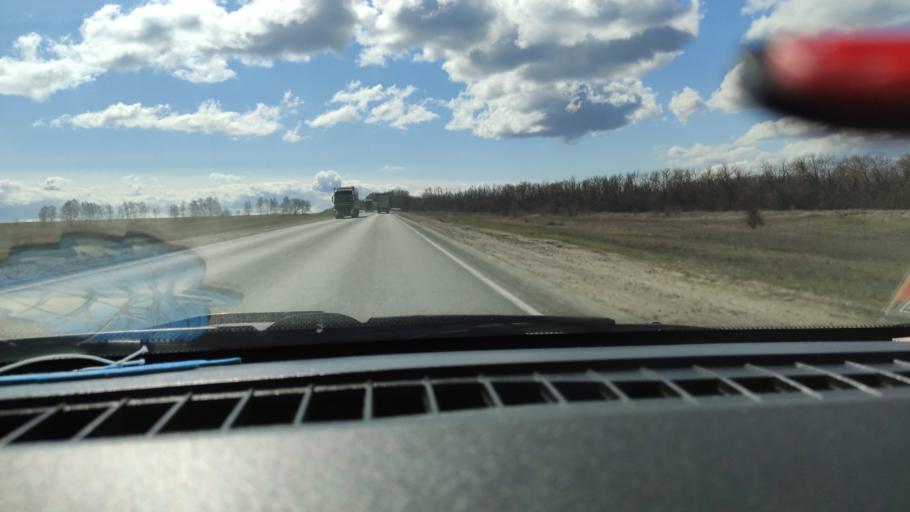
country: RU
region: Saratov
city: Dukhovnitskoye
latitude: 52.7272
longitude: 48.2599
